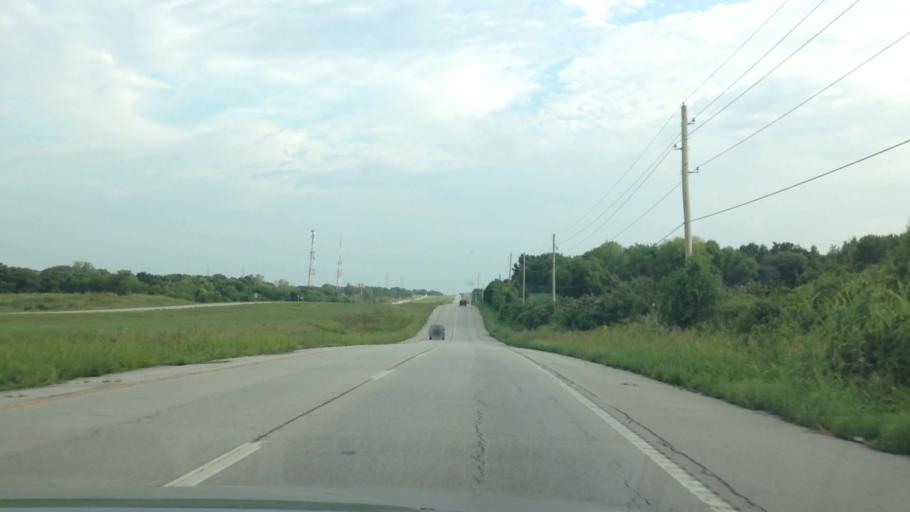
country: US
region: Missouri
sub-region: Clay County
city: Smithville
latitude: 39.3442
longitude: -94.5842
